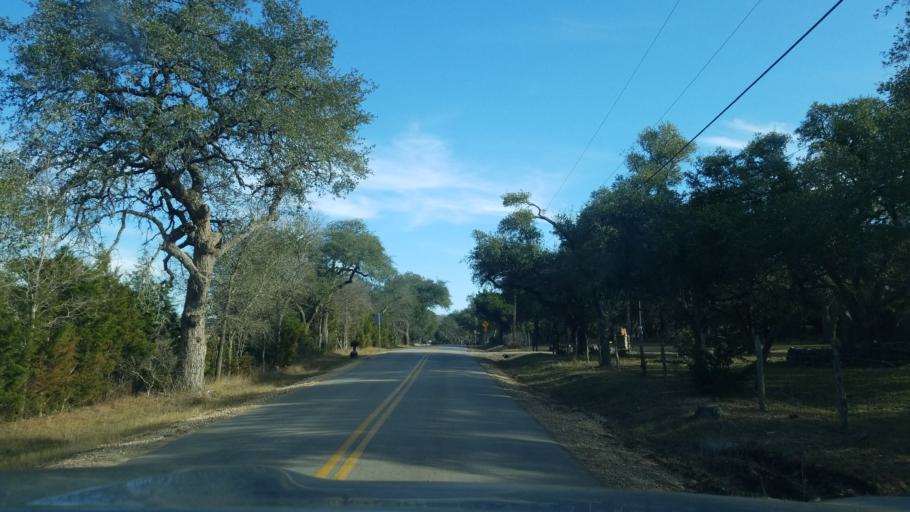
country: US
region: Texas
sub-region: Comal County
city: Canyon Lake
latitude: 29.7811
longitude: -98.2808
